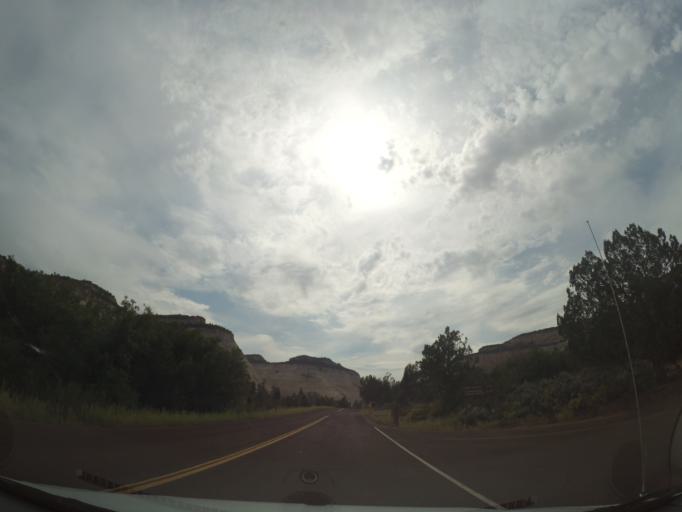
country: US
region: Utah
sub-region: Washington County
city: Hildale
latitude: 37.2331
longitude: -112.8759
